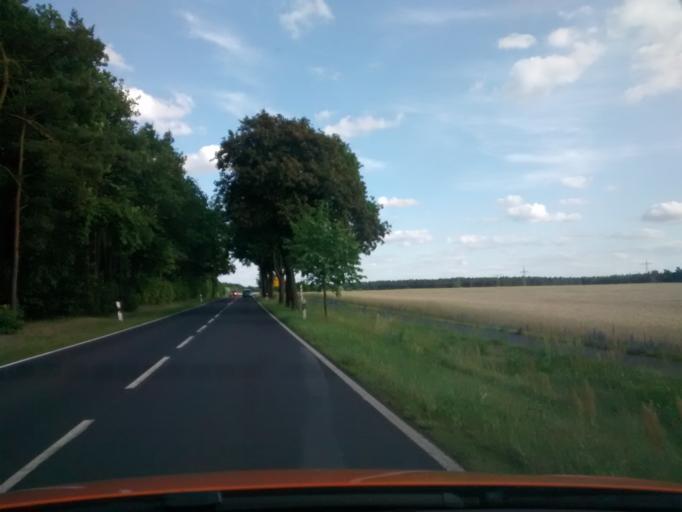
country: DE
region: Brandenburg
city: Ludwigsfelde
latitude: 52.2908
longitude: 13.2756
